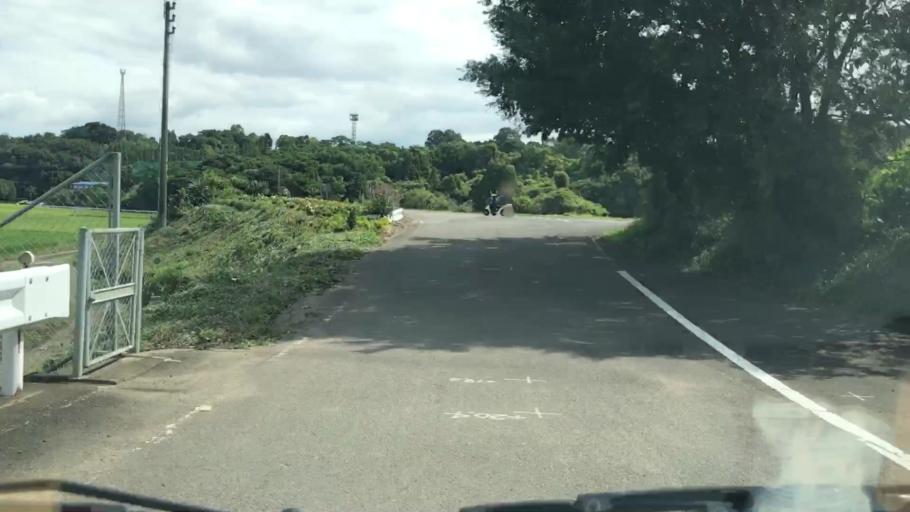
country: JP
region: Saga Prefecture
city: Saga-shi
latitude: 33.2330
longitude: 130.1727
